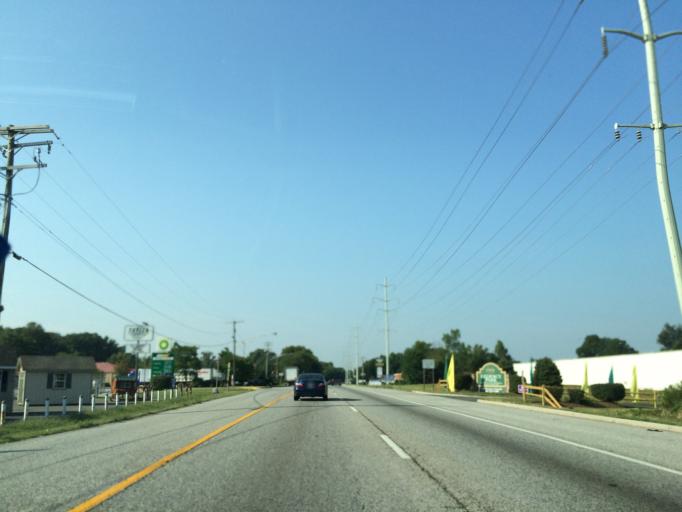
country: US
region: Maryland
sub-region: Anne Arundel County
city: Gambrills
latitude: 39.0518
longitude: -76.6617
